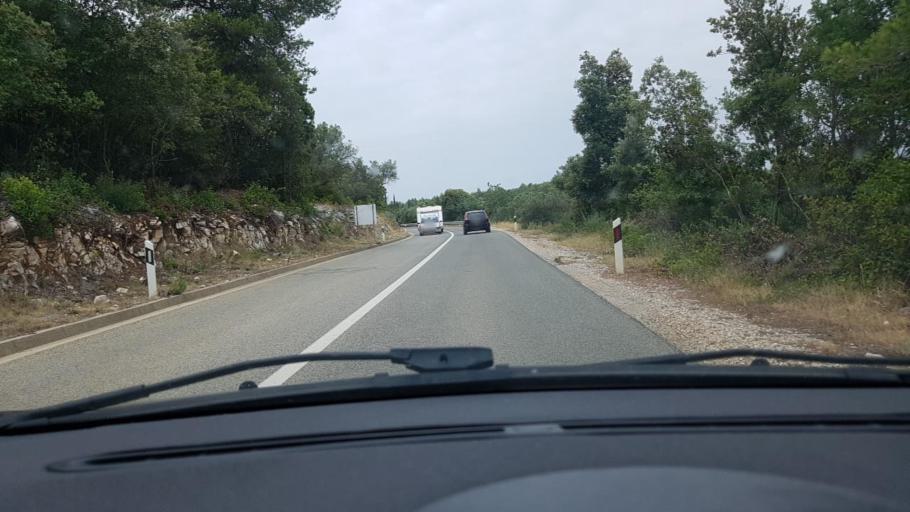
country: HR
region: Dubrovacko-Neretvanska
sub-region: Grad Korcula
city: Zrnovo
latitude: 42.9366
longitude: 17.0989
